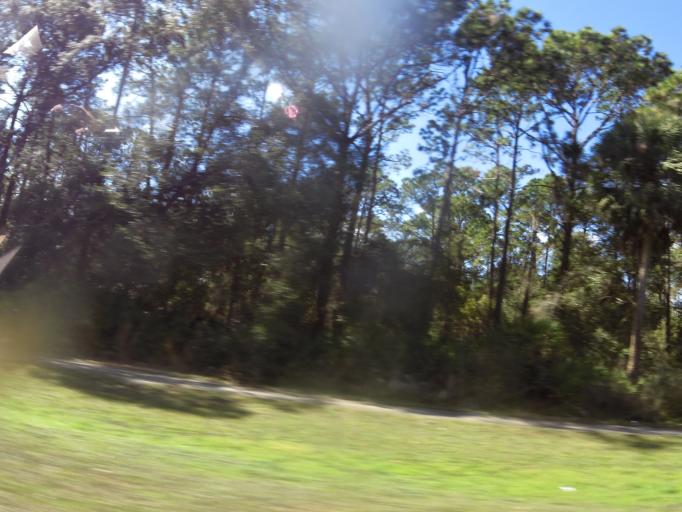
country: US
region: Florida
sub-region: Volusia County
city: Pierson
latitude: 29.2260
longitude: -81.4613
